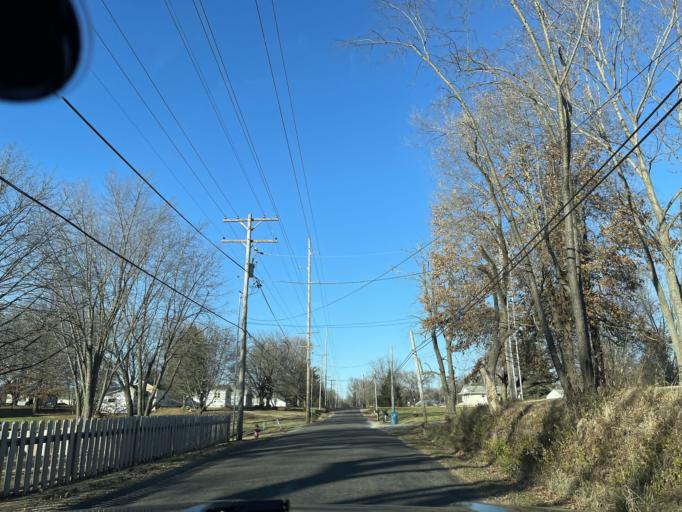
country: US
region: Illinois
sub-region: Sangamon County
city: Leland Grove
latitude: 39.8044
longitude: -89.7156
